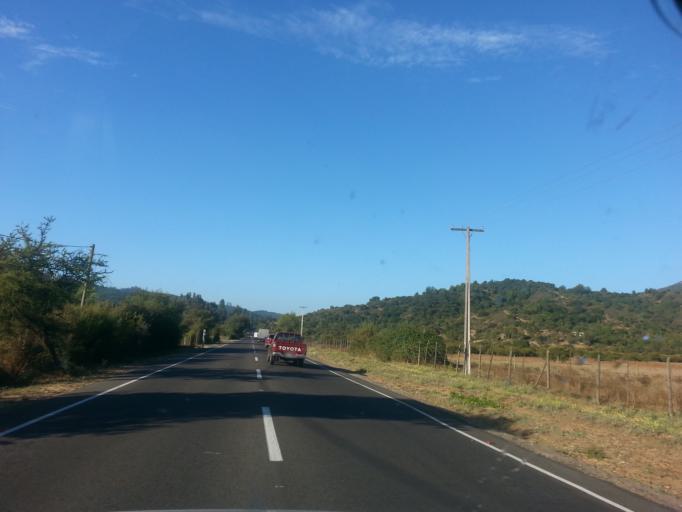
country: CL
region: Valparaiso
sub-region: Provincia de Marga Marga
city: Villa Alemana
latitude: -33.2203
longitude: -71.3916
